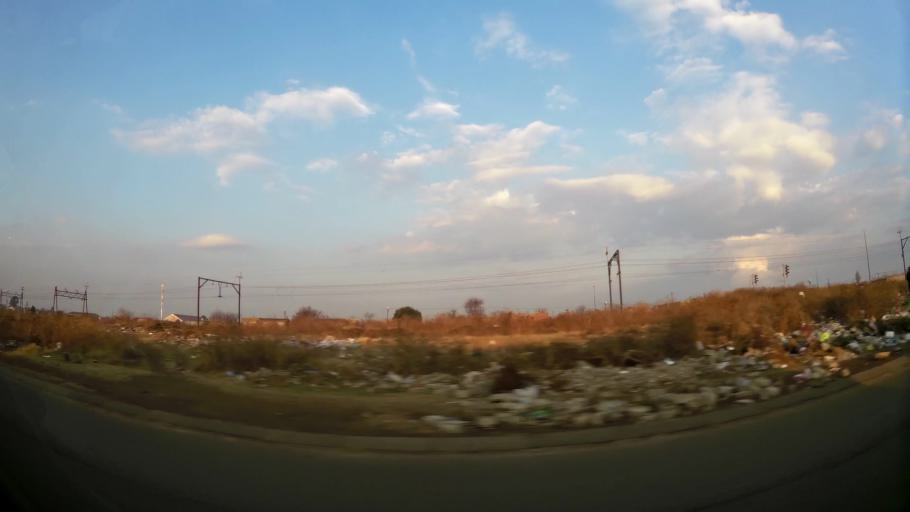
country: ZA
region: Gauteng
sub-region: City of Johannesburg Metropolitan Municipality
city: Orange Farm
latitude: -26.5484
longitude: 27.8856
